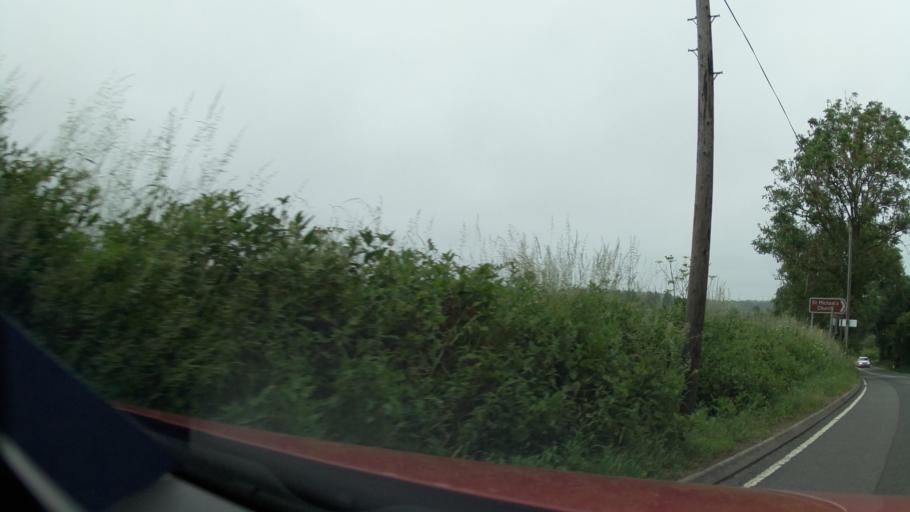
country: GB
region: England
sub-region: Derbyshire
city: Netherseal
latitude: 52.7036
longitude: -1.5548
